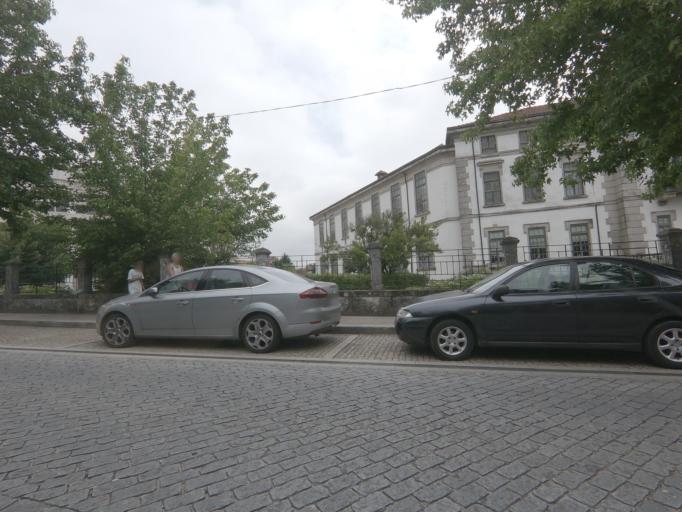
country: PT
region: Viana do Castelo
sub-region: Valenca
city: Valenca
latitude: 42.0261
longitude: -8.6420
